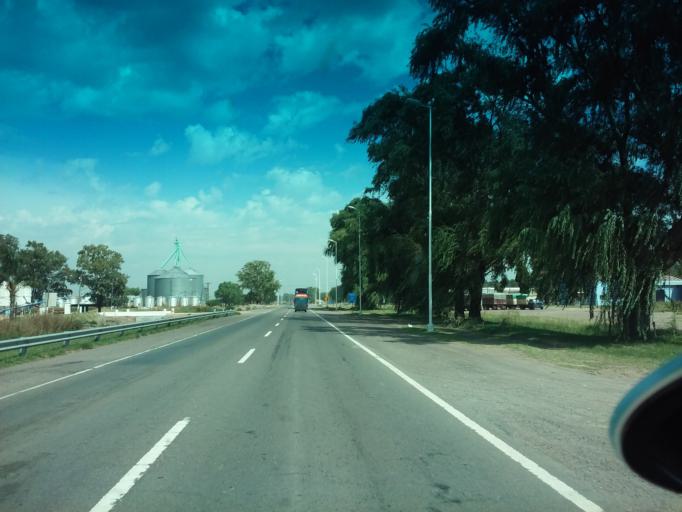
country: AR
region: Buenos Aires
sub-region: Partido de Carlos Casares
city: Carlos Casares
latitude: -35.6384
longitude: -61.3570
